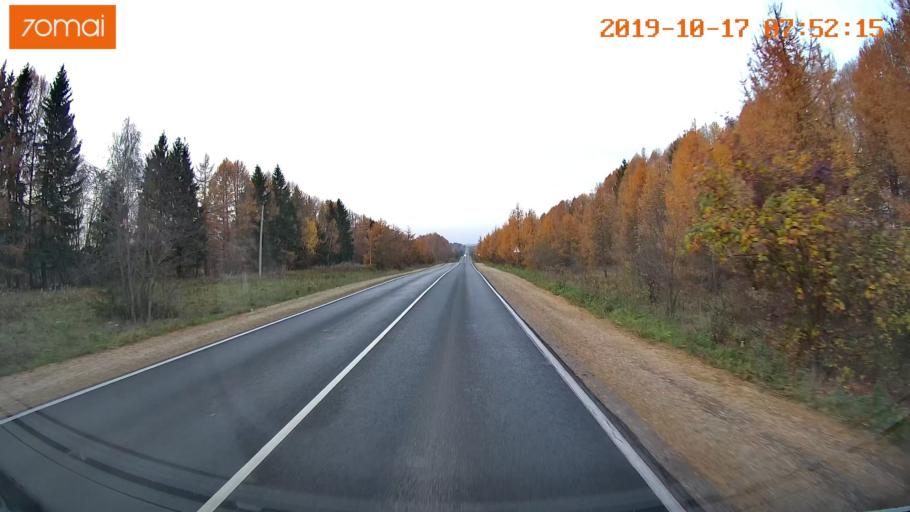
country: RU
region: Vladimir
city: Yur'yev-Pol'skiy
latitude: 56.4745
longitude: 39.6437
